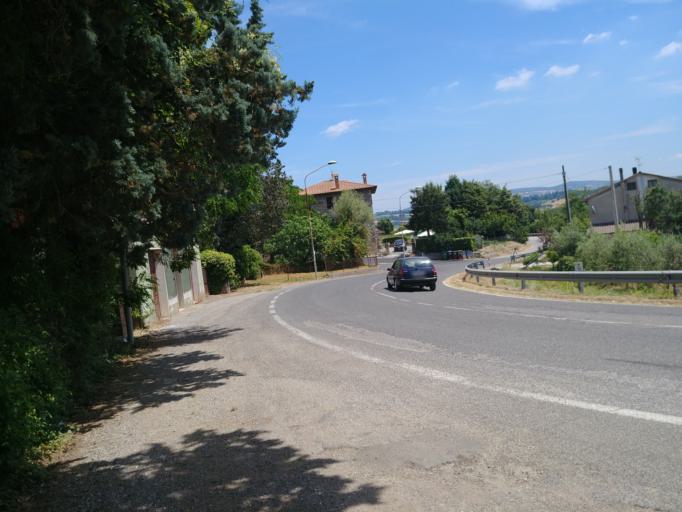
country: IT
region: Umbria
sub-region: Provincia di Perugia
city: Monte Castello di Vibio
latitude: 42.8325
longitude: 12.3723
